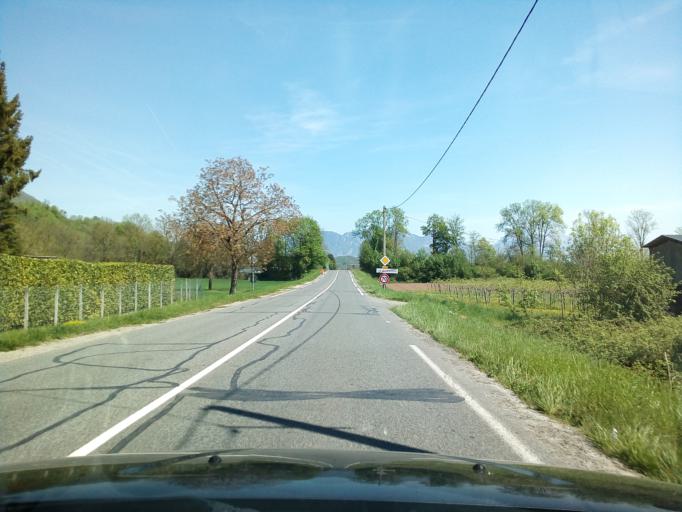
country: FR
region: Rhone-Alpes
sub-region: Departement de l'Isere
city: Barraux
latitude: 45.4053
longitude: 5.9807
